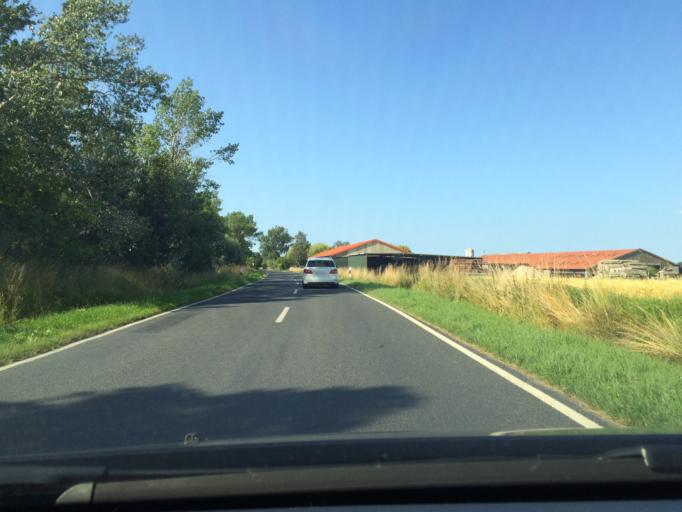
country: DE
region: Mecklenburg-Vorpommern
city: Velgast
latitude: 54.3226
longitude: 12.7943
